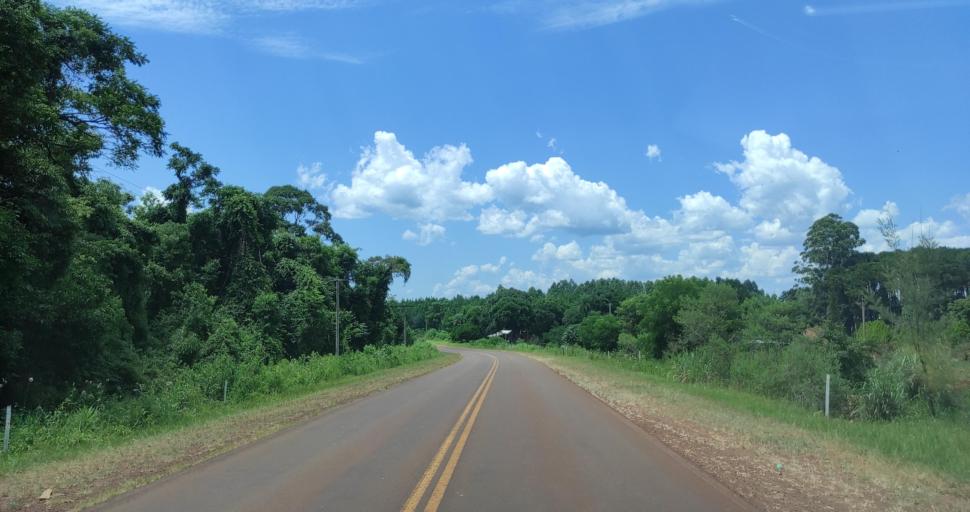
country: AR
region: Misiones
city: Ruiz de Montoya
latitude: -27.0017
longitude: -55.0426
